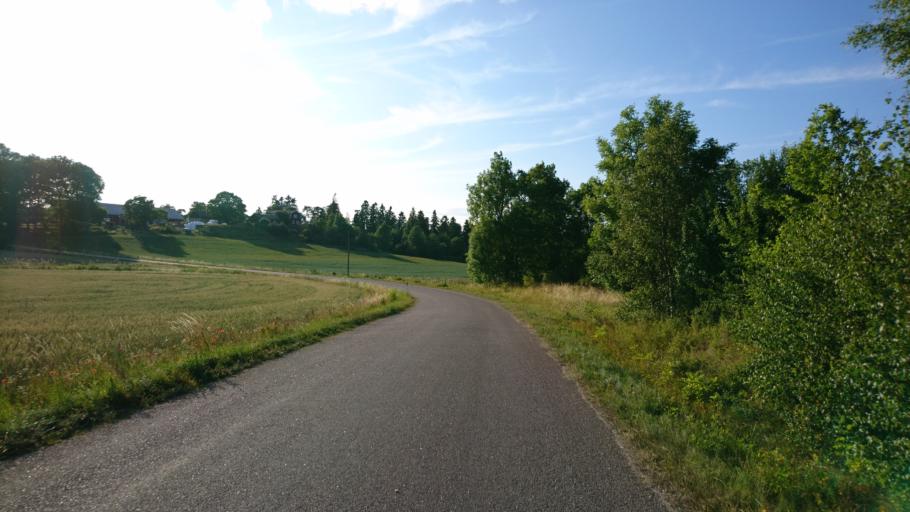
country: SE
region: Soedermanland
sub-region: Strangnas Kommun
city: Stallarholmen
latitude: 59.4019
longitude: 17.2985
